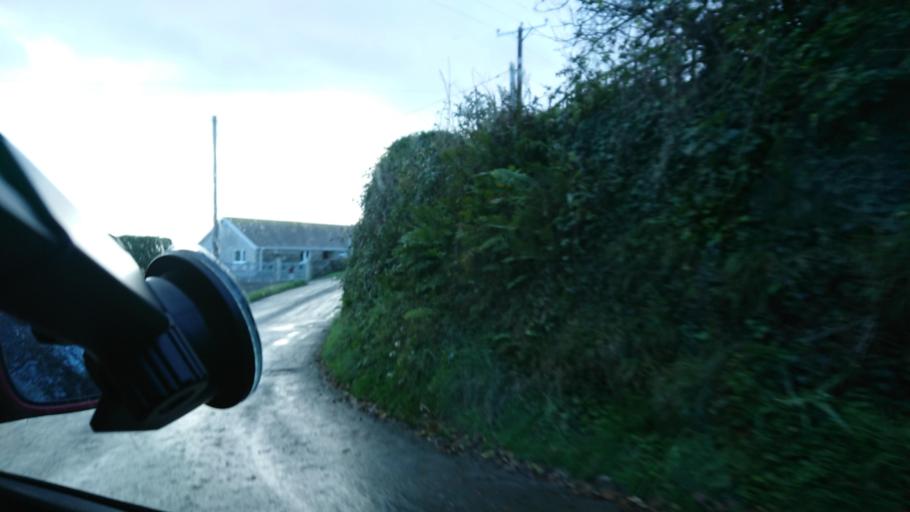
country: GB
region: England
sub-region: Cornwall
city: Looe
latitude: 50.3481
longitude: -4.4737
